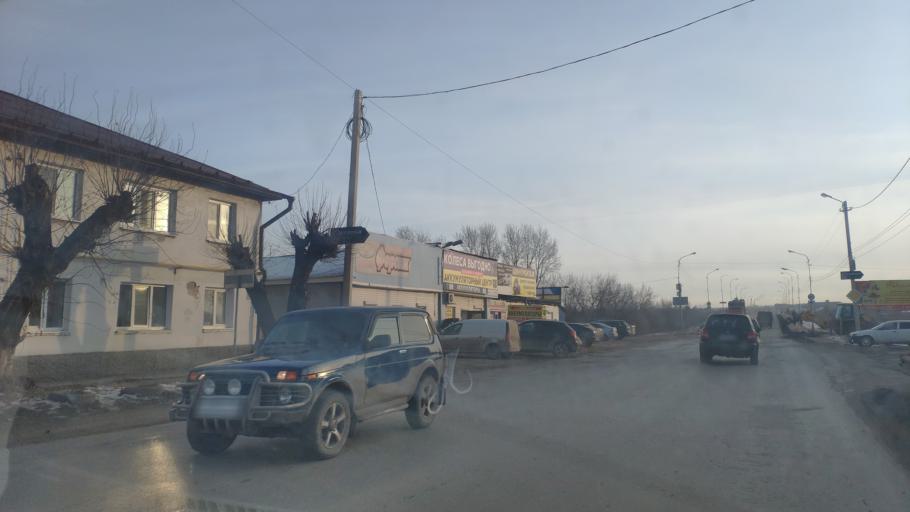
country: RU
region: Kurgan
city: Shadrinsk
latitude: 56.0779
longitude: 63.6412
